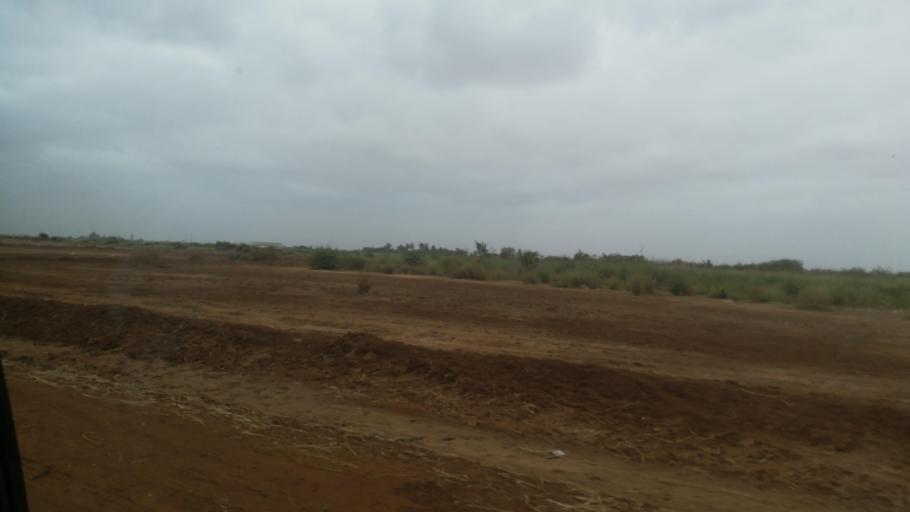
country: SN
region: Saint-Louis
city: Rosso
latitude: 16.2803
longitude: -16.1608
